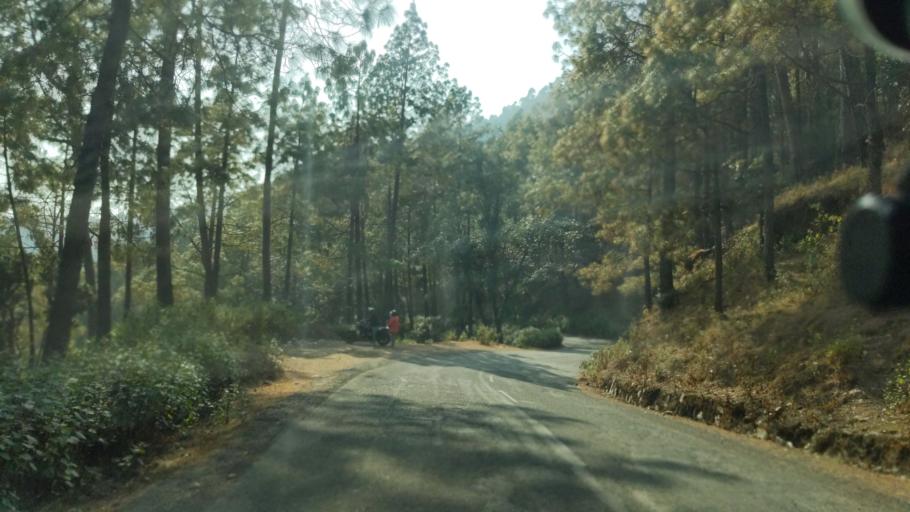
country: IN
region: Uttarakhand
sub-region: Naini Tal
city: Bhowali
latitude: 29.4039
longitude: 79.5394
